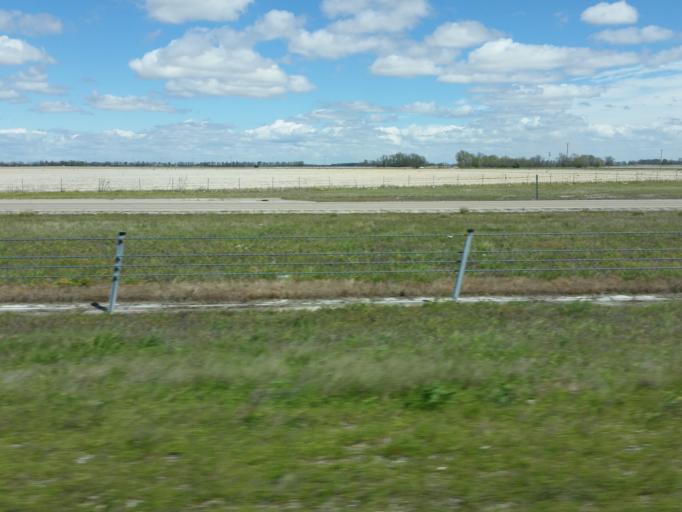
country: US
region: Arkansas
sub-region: Craighead County
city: Bay
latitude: 35.7770
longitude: -90.5889
